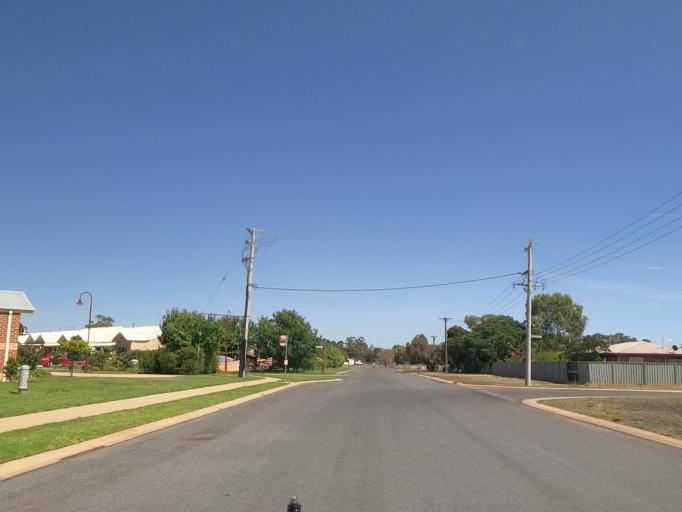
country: AU
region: New South Wales
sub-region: Corowa Shire
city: Mulwala
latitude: -35.9858
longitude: 146.0035
